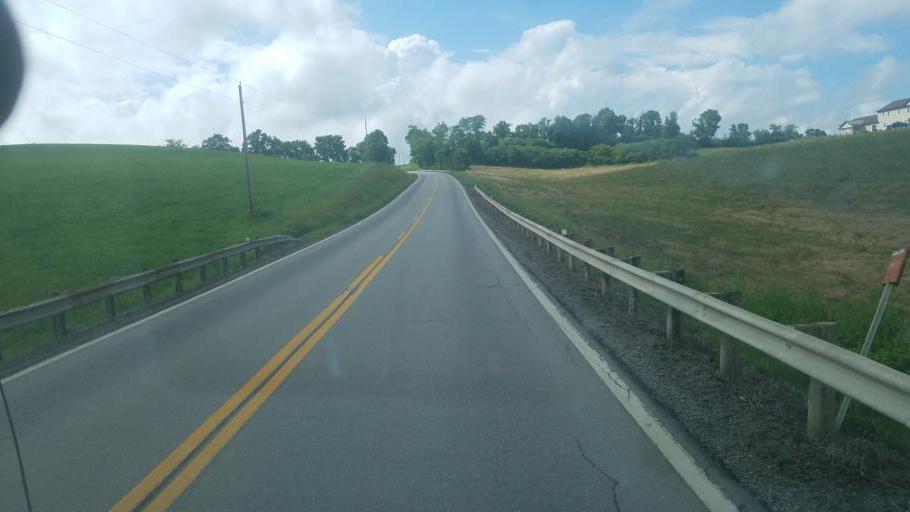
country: US
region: Ohio
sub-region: Carroll County
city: Carrollton
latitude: 40.4462
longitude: -80.9796
